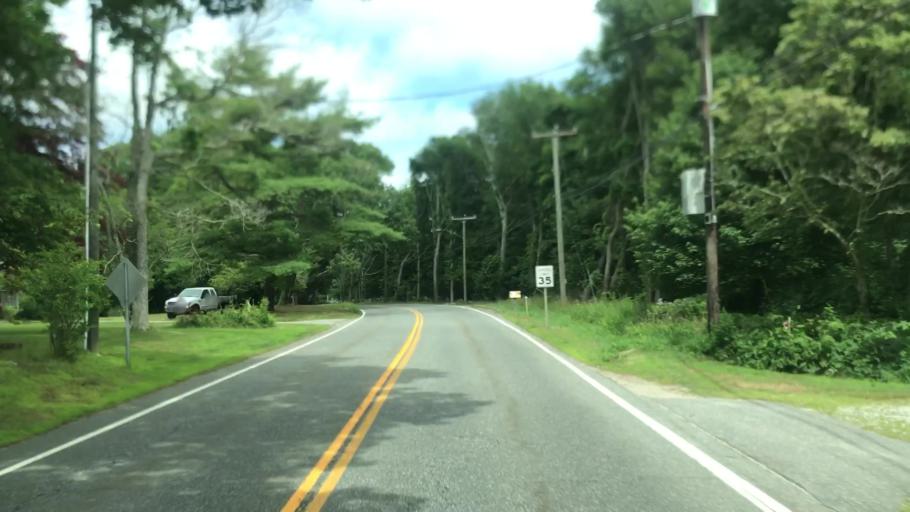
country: US
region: Connecticut
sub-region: New London County
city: Niantic
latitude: 41.2902
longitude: -72.2707
